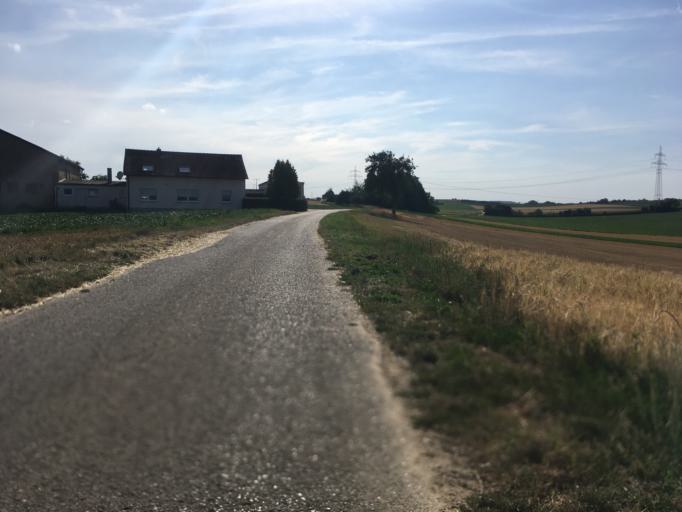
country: DE
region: Baden-Wuerttemberg
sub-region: Regierungsbezirk Stuttgart
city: Untereisesheim
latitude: 49.1955
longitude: 9.1837
